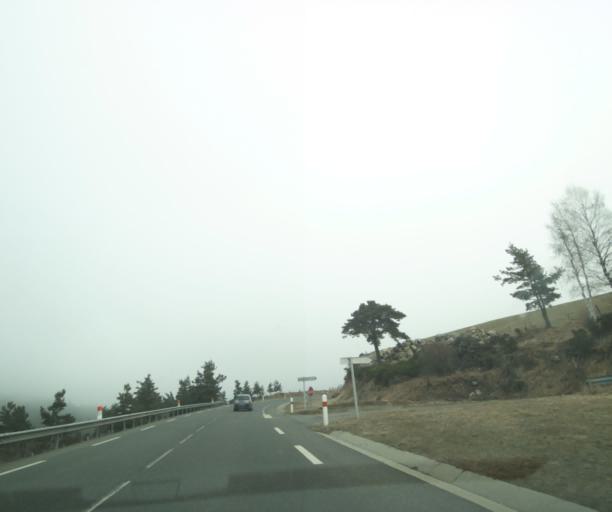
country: FR
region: Languedoc-Roussillon
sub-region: Departement de la Lozere
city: Langogne
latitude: 44.6743
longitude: 3.7654
